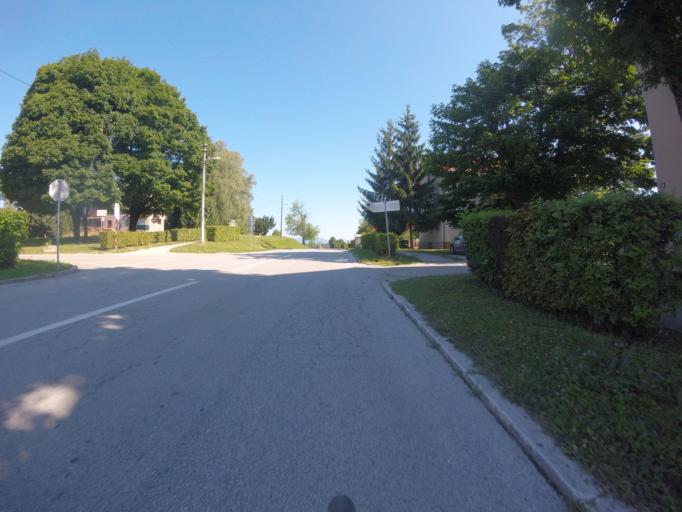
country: HR
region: Zagrebacka
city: Bregana
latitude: 45.8385
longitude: 15.6880
